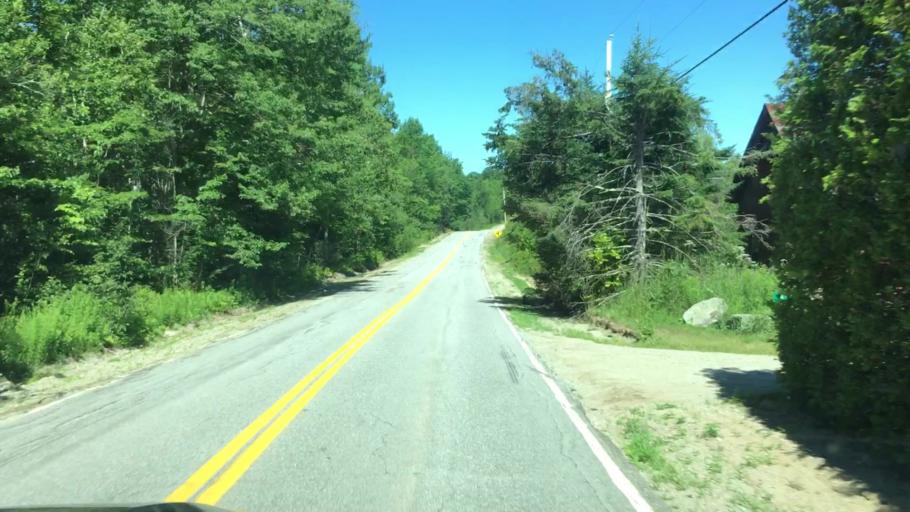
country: US
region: Maine
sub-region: Hancock County
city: Penobscot
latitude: 44.4244
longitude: -68.7080
